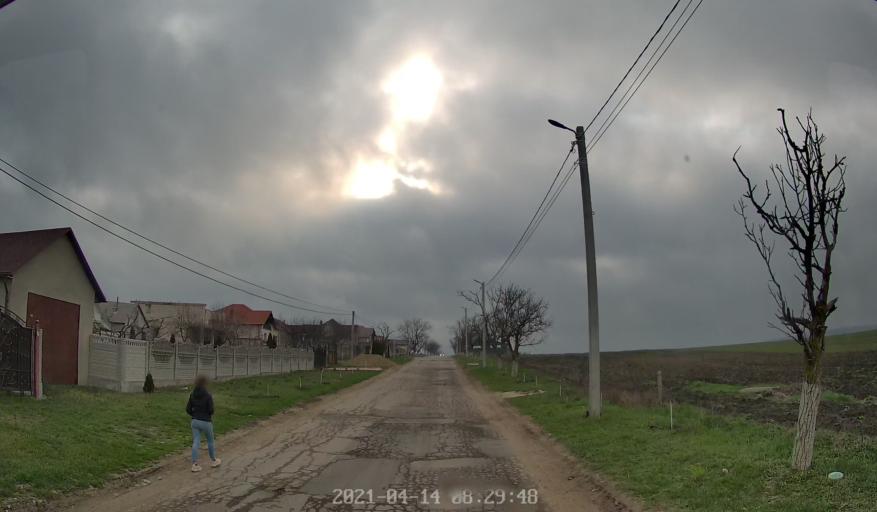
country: MD
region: Chisinau
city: Stauceni
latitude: 47.0635
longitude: 28.9249
